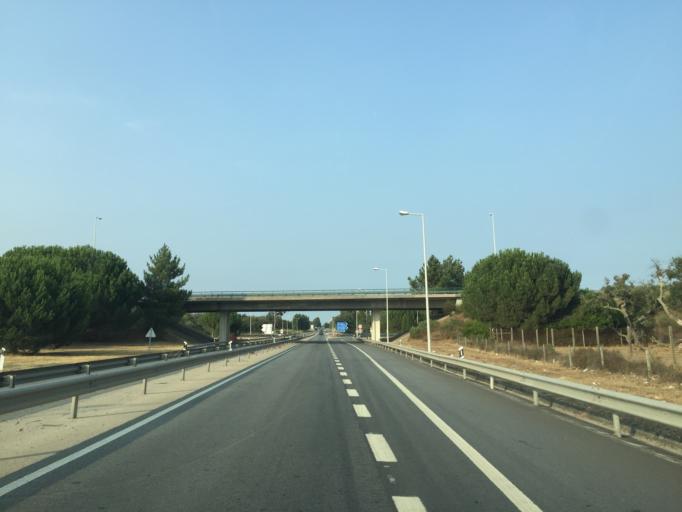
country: PT
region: Setubal
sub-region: Setubal
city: Setubal
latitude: 38.5937
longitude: -8.6725
